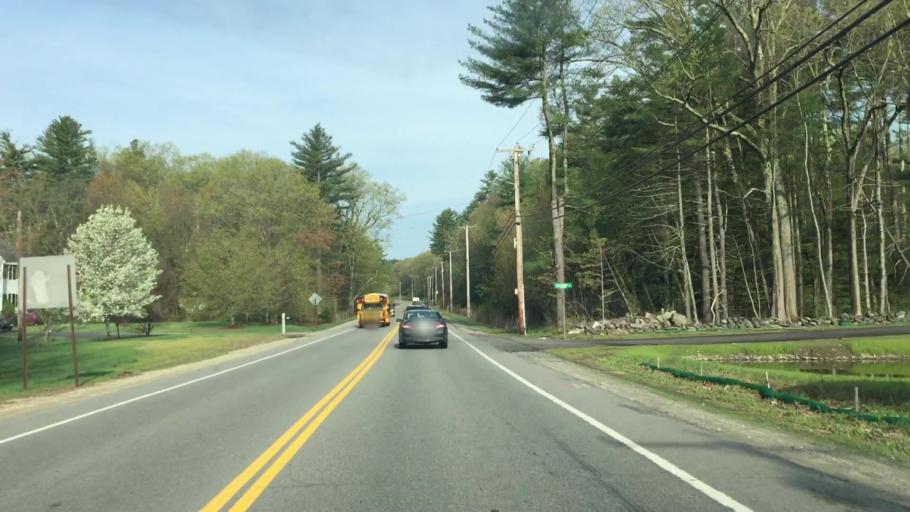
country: US
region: New Hampshire
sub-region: Hillsborough County
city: Pelham
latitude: 42.7032
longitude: -71.3546
